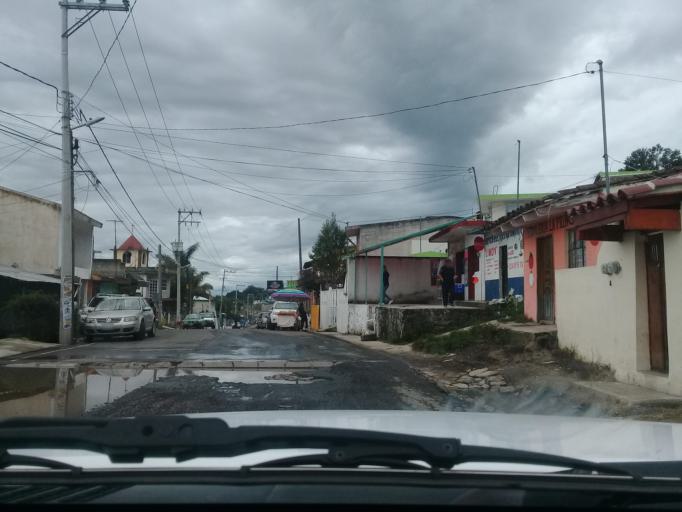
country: MX
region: Veracruz
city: Rafael Lucio
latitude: 19.5991
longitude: -96.9895
